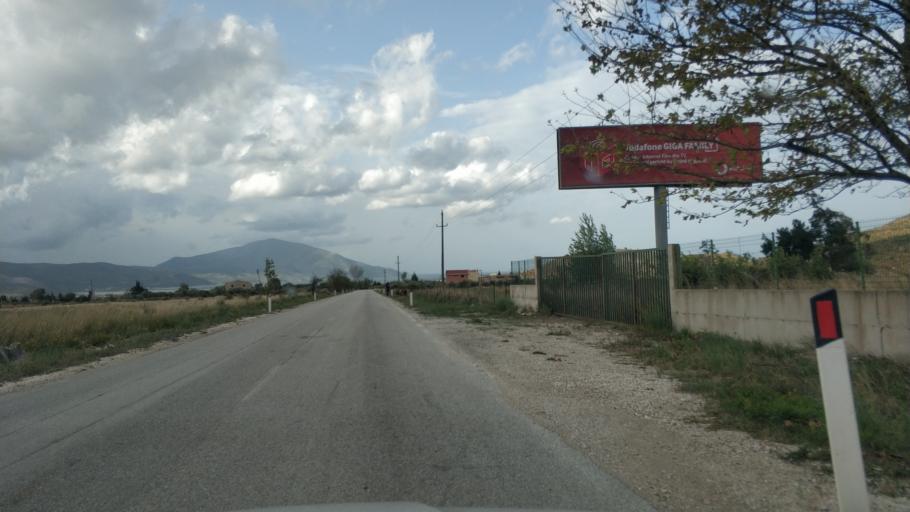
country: AL
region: Vlore
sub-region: Rrethi i Vlores
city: Orikum
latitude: 40.2866
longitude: 19.4956
